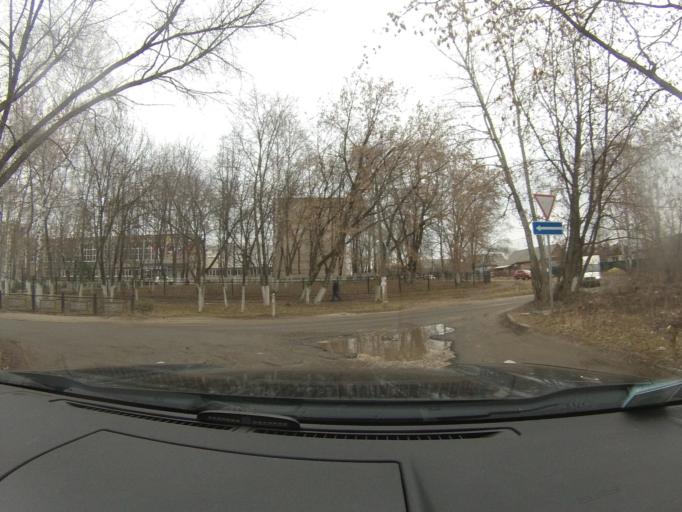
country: RU
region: Moskovskaya
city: Peski
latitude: 55.2693
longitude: 38.7479
